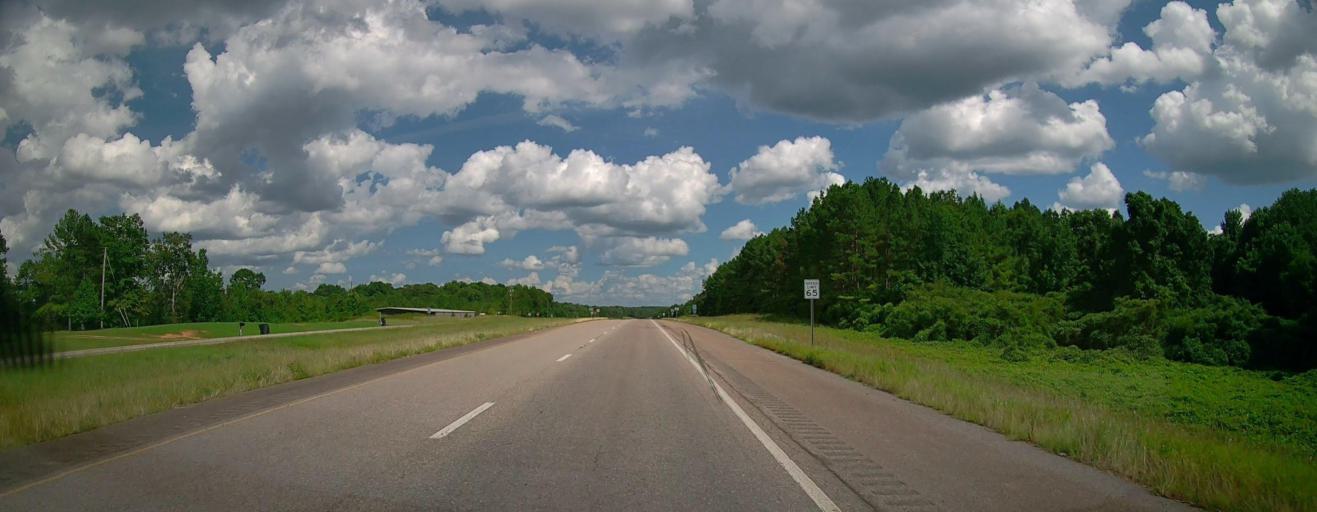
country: US
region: Mississippi
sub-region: Lowndes County
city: New Hope
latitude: 33.4738
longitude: -88.2457
